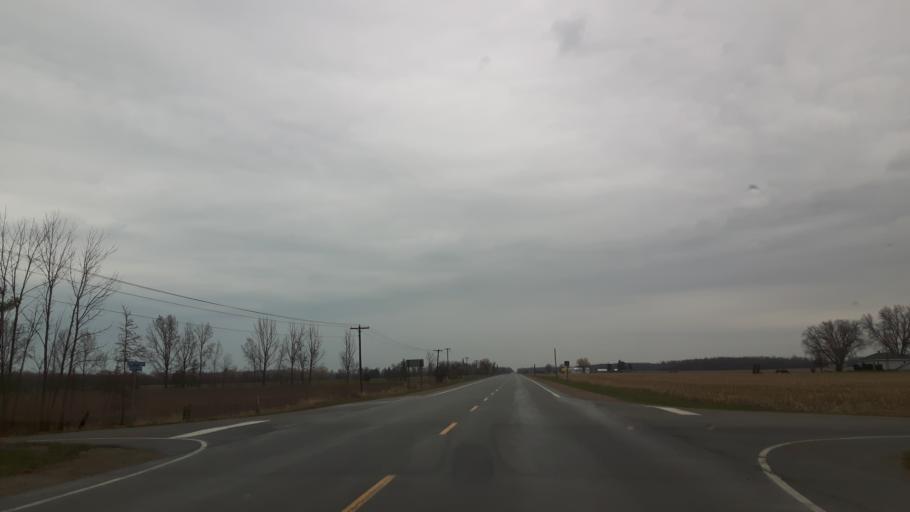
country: CA
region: Ontario
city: Goderich
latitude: 43.6239
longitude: -81.7056
